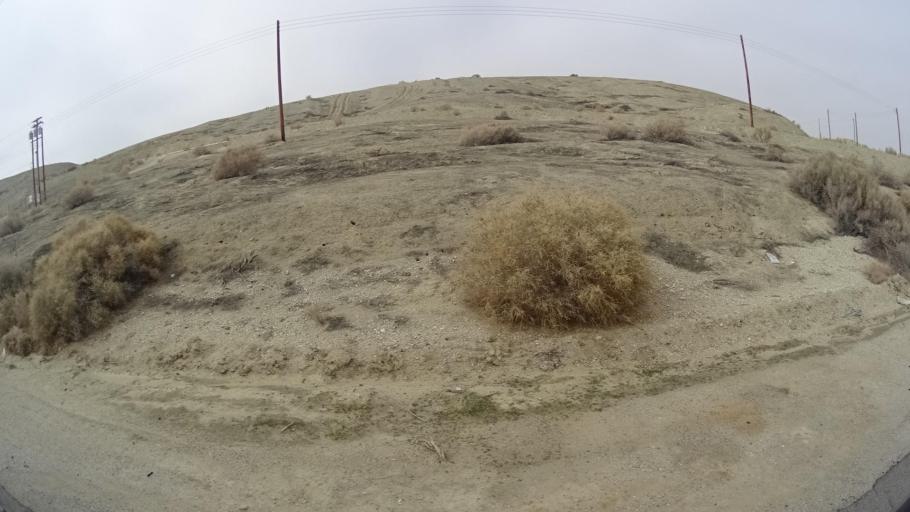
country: US
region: California
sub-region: Kern County
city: Maricopa
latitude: 35.0805
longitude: -119.3990
